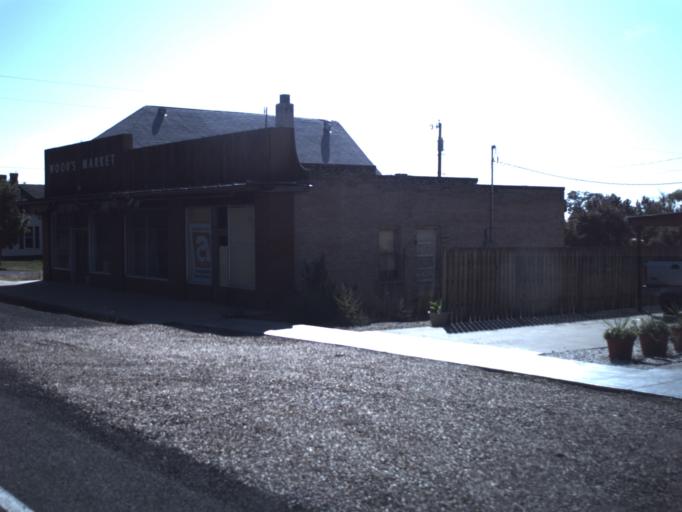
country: US
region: Utah
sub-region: Millard County
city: Fillmore
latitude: 39.0998
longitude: -112.2710
